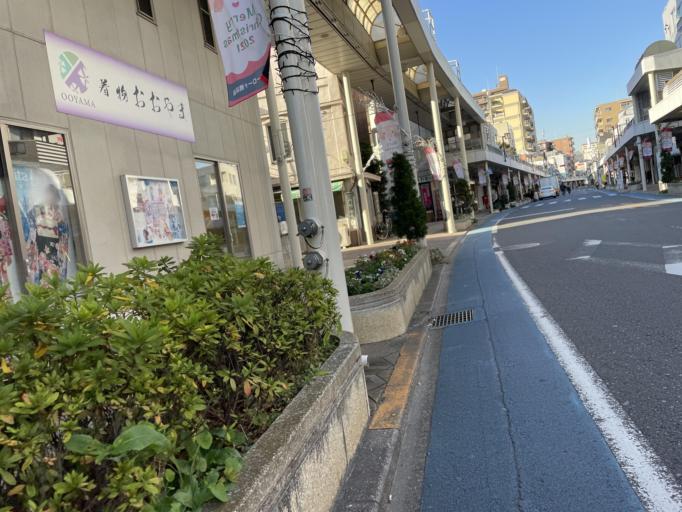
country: JP
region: Tokyo
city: Urayasu
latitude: 35.7264
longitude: 139.8825
